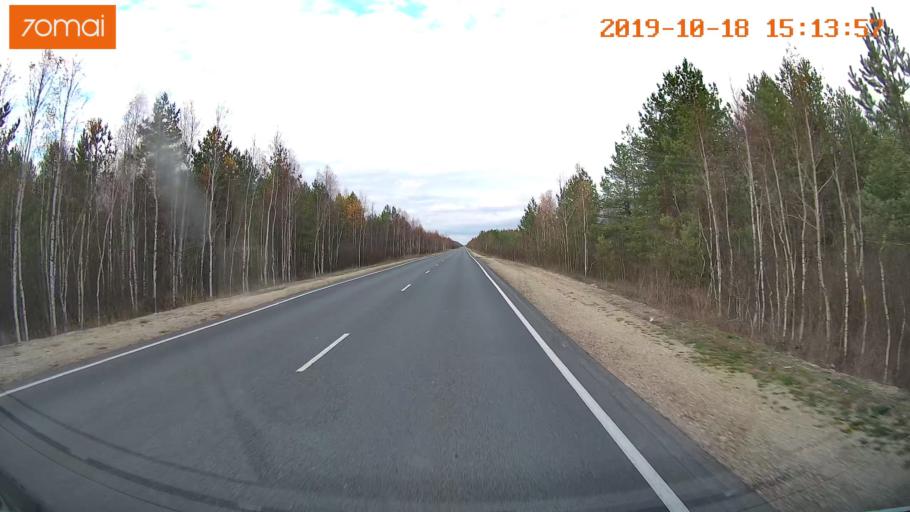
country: RU
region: Vladimir
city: Gus'-Khrustal'nyy
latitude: 55.5948
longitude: 40.7192
